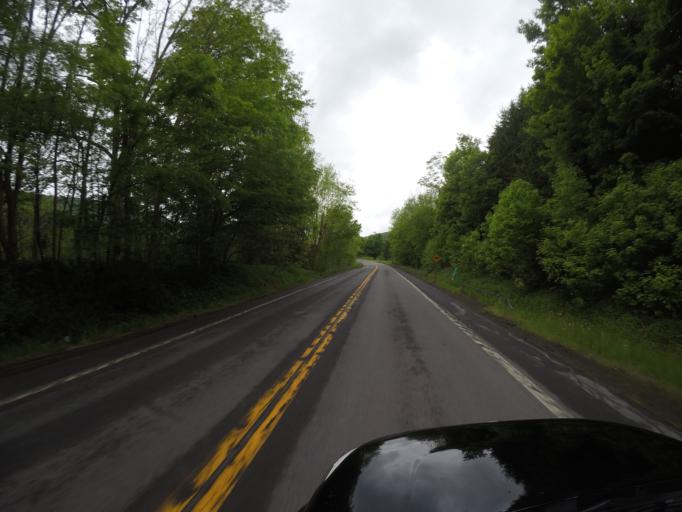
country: US
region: New York
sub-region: Delaware County
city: Delhi
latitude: 42.2588
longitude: -74.8778
